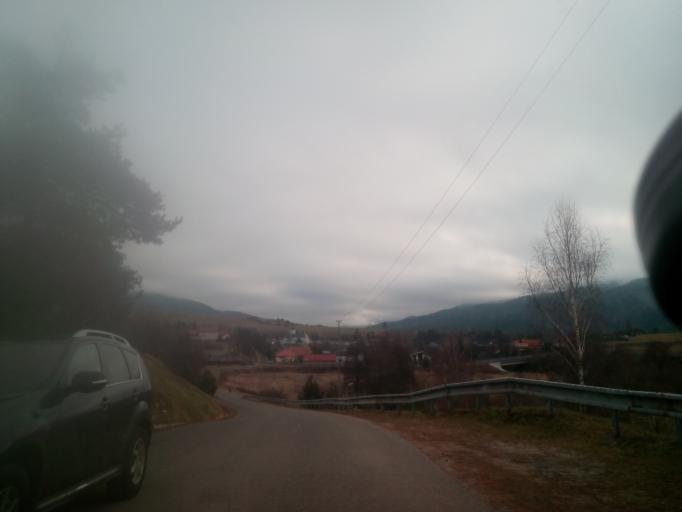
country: SK
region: Kosicky
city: Krompachy
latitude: 48.9248
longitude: 20.9288
